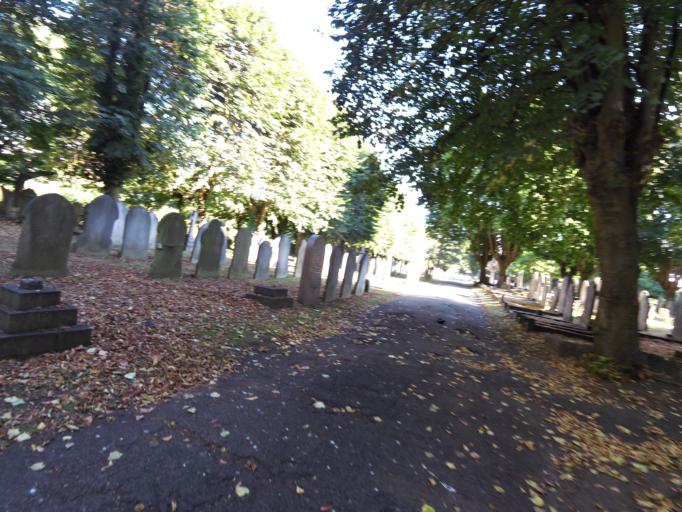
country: GB
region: England
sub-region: Greater London
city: Harringay
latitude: 51.6024
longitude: -0.0779
